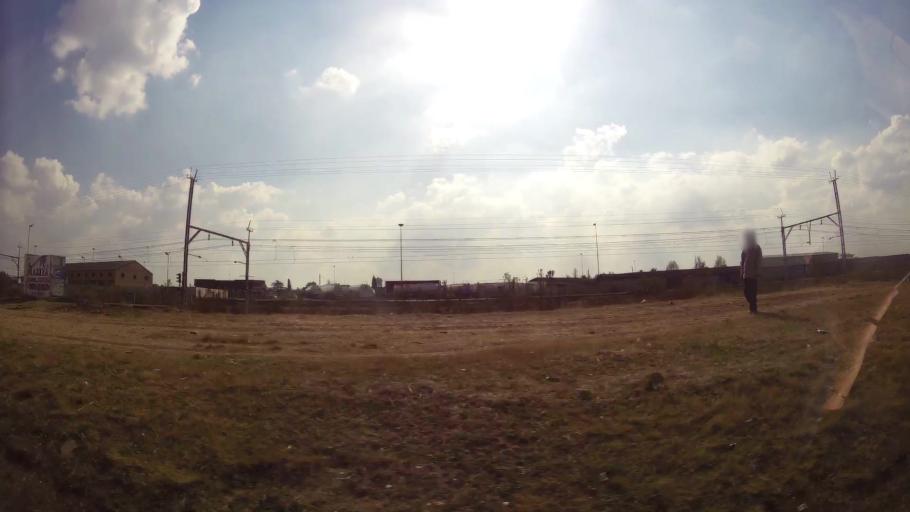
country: ZA
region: Gauteng
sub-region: Ekurhuleni Metropolitan Municipality
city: Germiston
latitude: -26.3256
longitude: 28.1601
